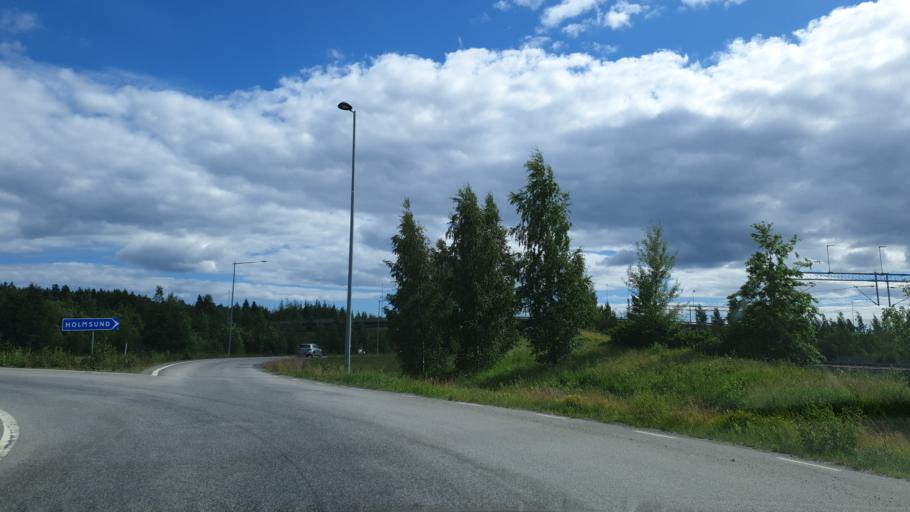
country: SE
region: Vaesterbotten
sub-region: Umea Kommun
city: Umea
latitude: 63.7920
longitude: 20.3123
